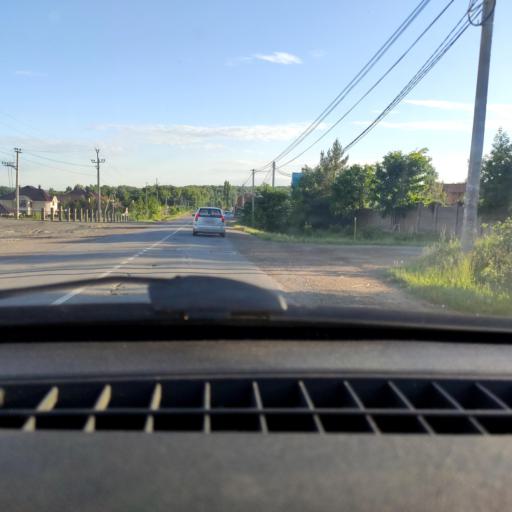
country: RU
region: Bashkortostan
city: Avdon
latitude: 54.6435
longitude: 55.7041
